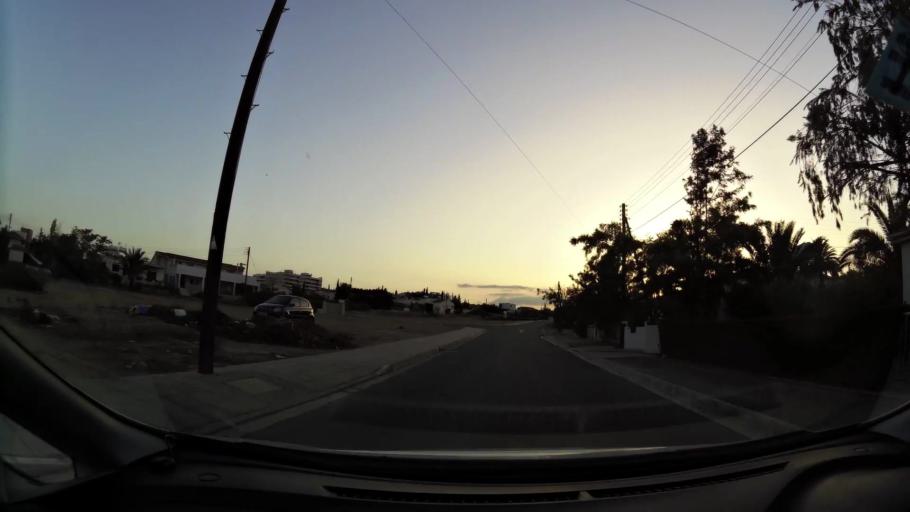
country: CY
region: Lefkosia
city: Nicosia
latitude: 35.1568
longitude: 33.3244
